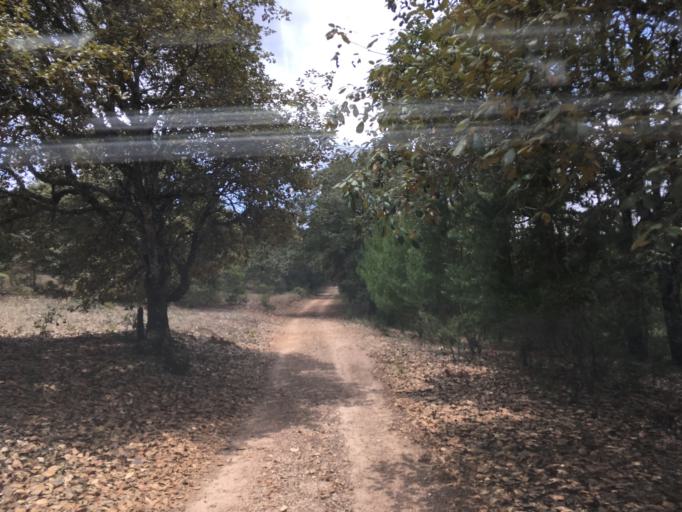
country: MX
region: Oaxaca
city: San Andres Sinaxtla
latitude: 17.6064
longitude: -97.2667
